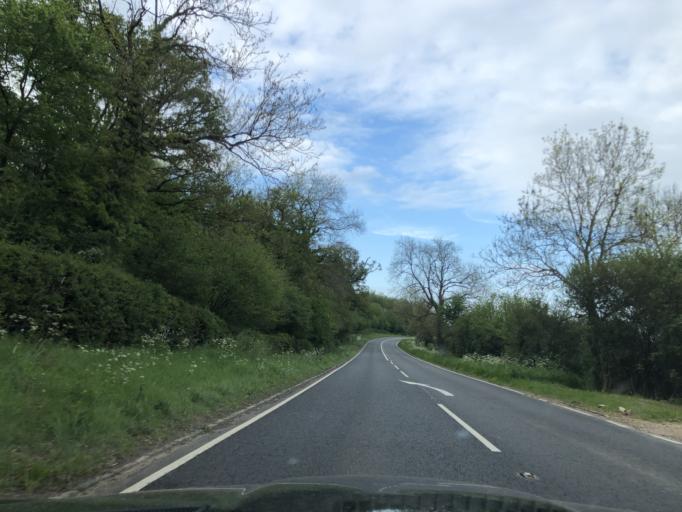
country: GB
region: England
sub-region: Gloucestershire
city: Moreton in Marsh
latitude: 52.0089
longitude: -1.6938
